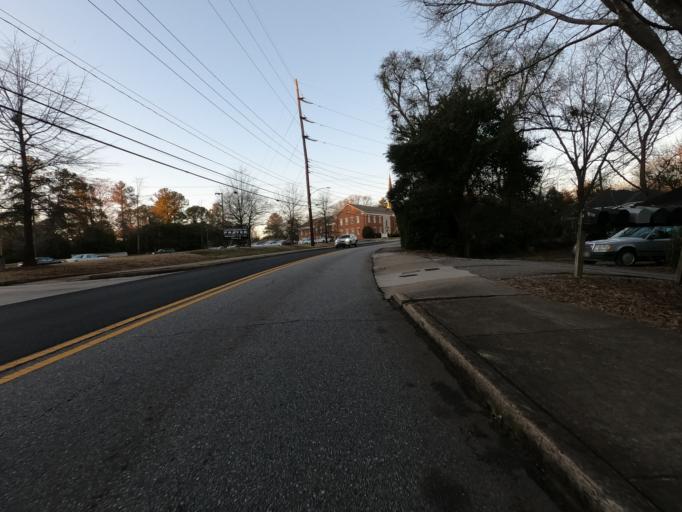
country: US
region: Georgia
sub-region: Clarke County
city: Athens
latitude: 33.9311
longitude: -83.3928
